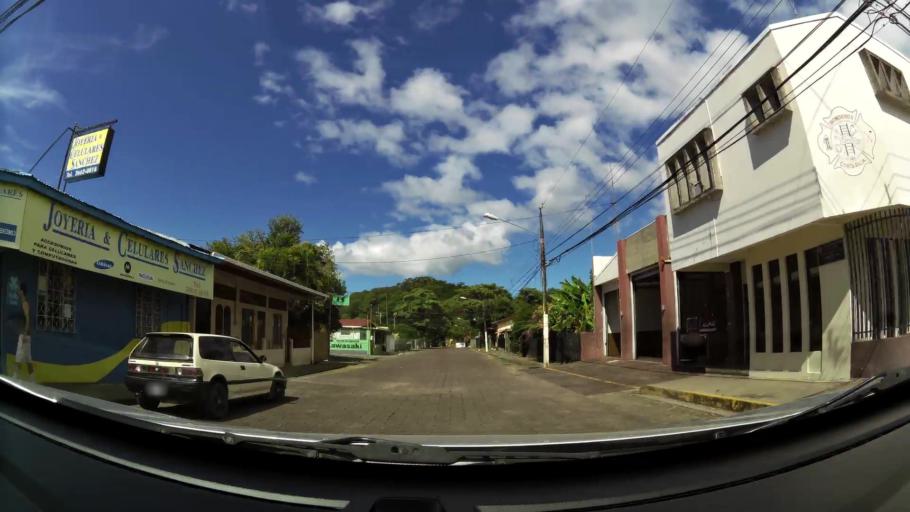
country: CR
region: Guanacaste
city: Juntas
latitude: 10.2816
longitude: -84.9588
